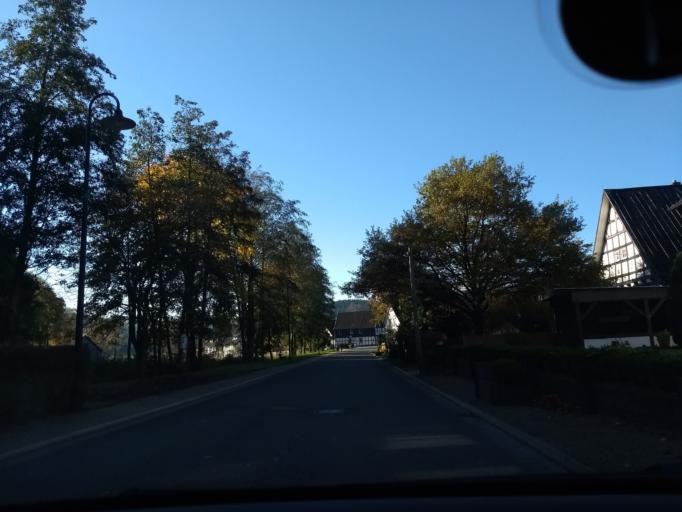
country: DE
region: North Rhine-Westphalia
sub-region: Regierungsbezirk Arnsberg
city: Lennestadt
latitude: 51.2097
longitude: 8.0735
